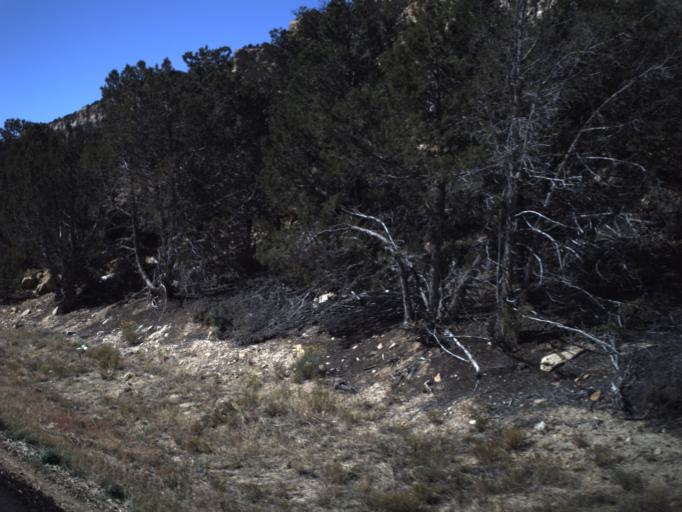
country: US
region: Utah
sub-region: Wayne County
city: Loa
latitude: 37.7326
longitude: -111.7554
